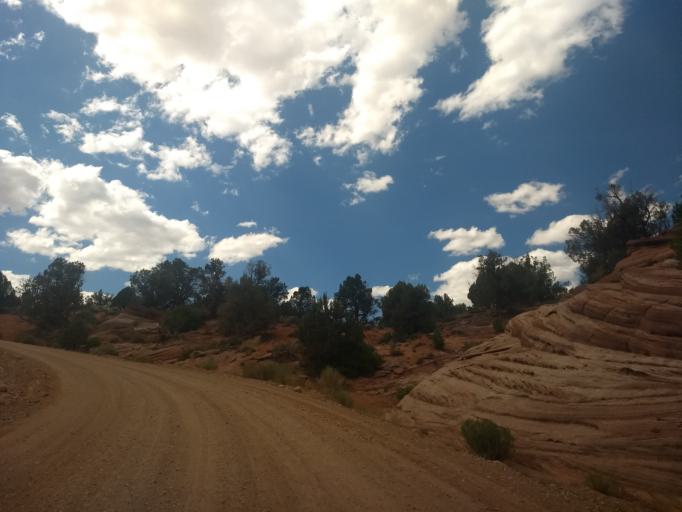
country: US
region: Utah
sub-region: Kane County
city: Kanab
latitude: 37.1519
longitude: -112.5417
